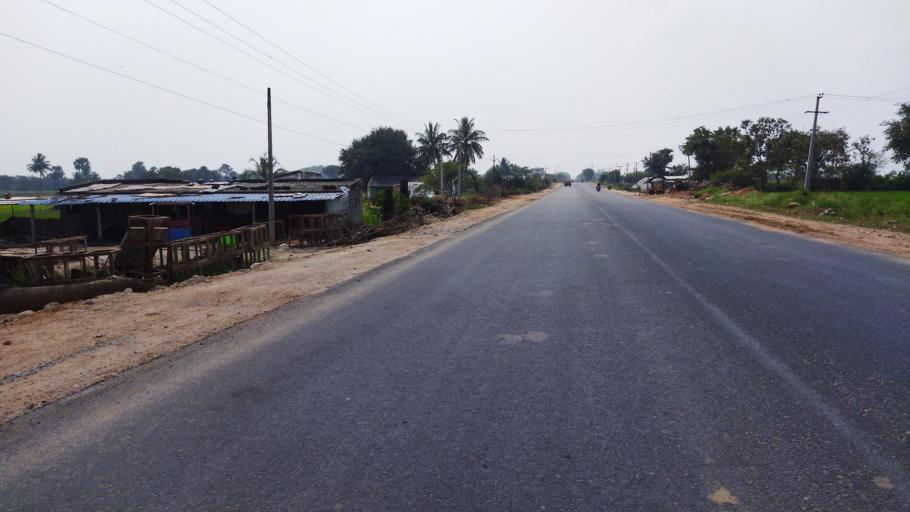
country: IN
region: Telangana
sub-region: Nalgonda
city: Nalgonda
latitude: 17.0868
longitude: 79.3260
